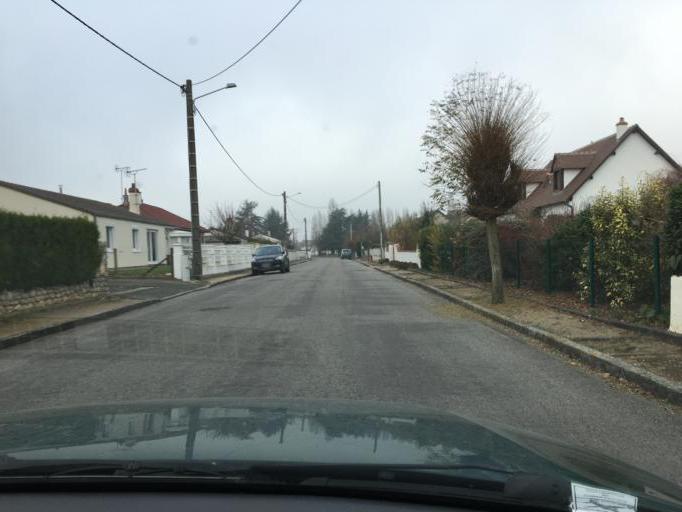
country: FR
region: Centre
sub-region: Departement du Loiret
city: Gidy
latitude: 47.9863
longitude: 1.8419
